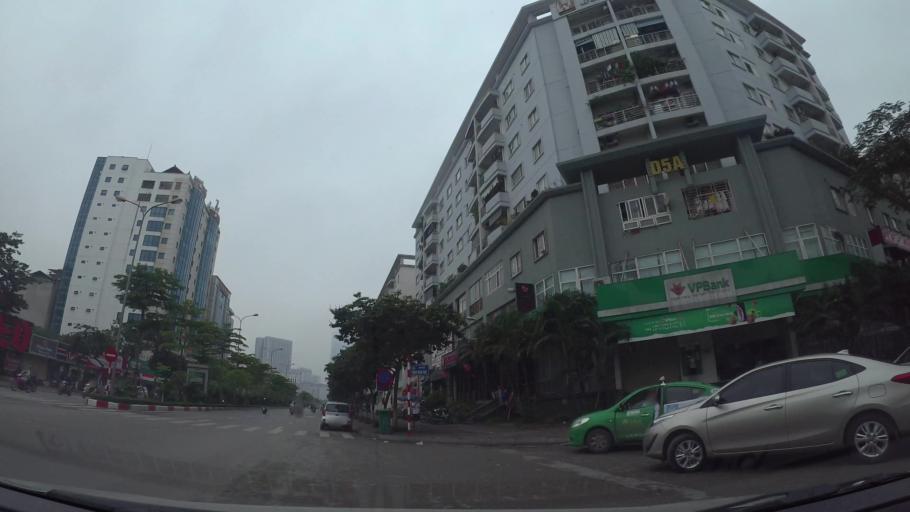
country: VN
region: Ha Noi
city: Cau Giay
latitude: 21.0332
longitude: 105.7886
